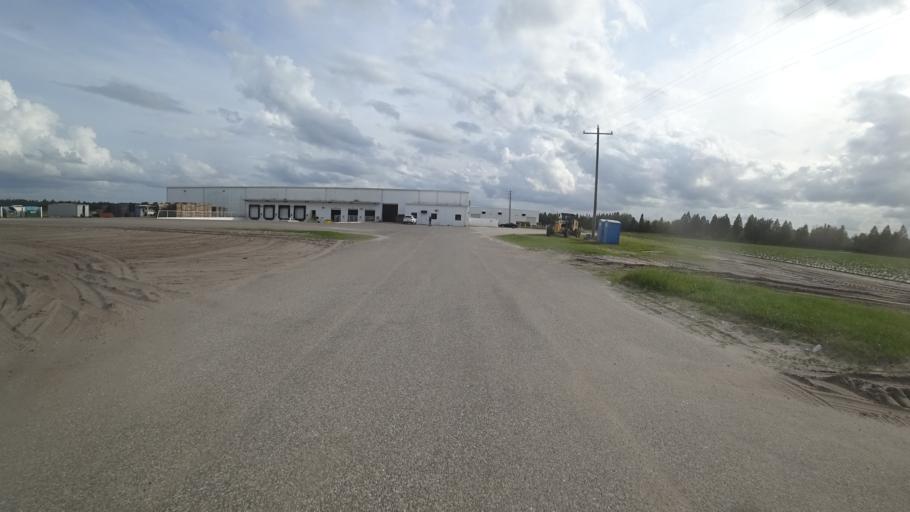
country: US
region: Florida
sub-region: Hillsborough County
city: Wimauma
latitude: 27.5868
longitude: -82.1589
